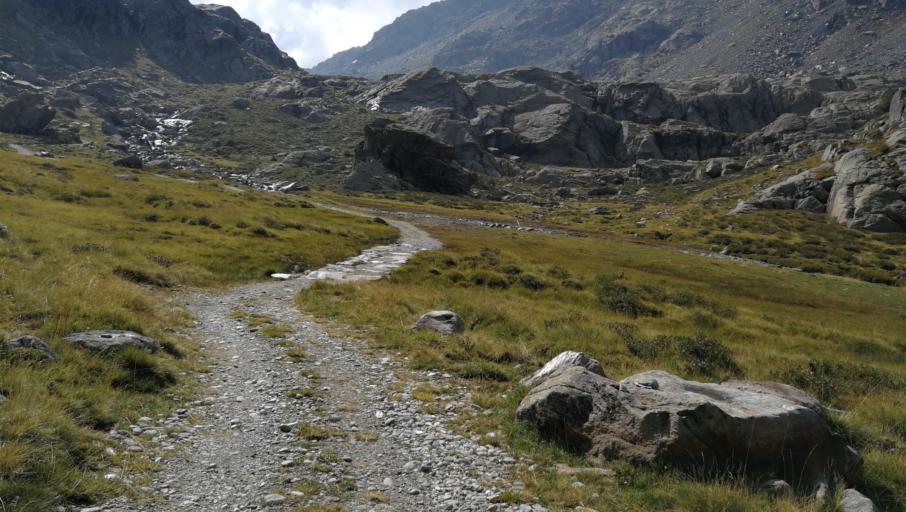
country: CH
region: Grisons
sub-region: Bernina District
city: Poschiavo
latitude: 46.3177
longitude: 9.9672
